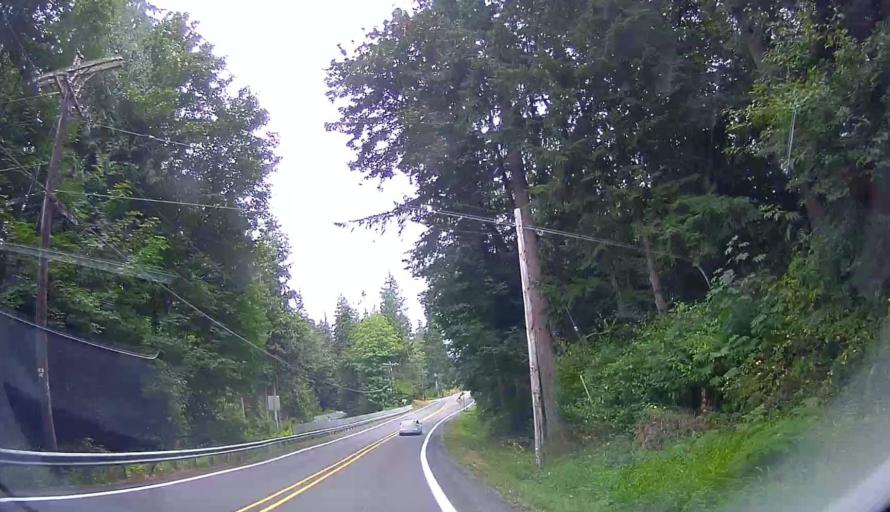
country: US
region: Washington
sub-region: Snohomish County
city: Warm Beach
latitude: 48.1371
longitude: -122.3610
